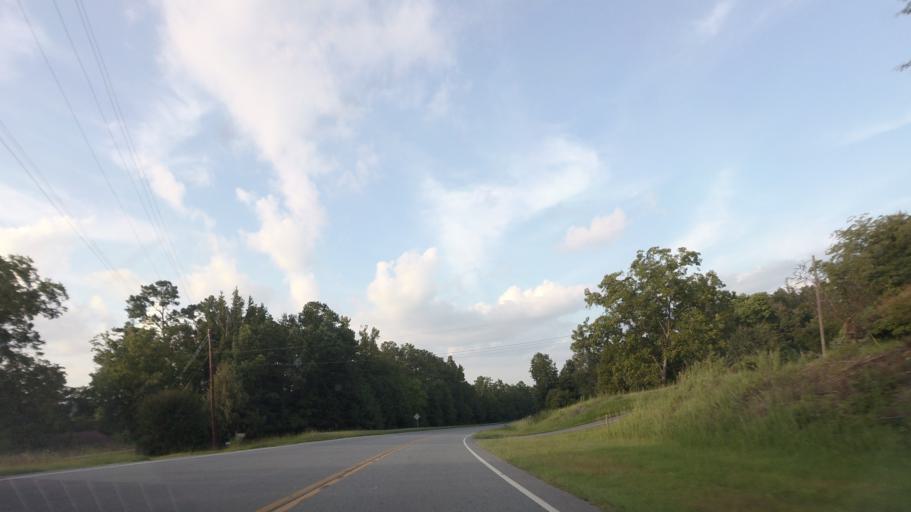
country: US
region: Georgia
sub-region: Wilkinson County
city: Gordon
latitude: 32.8638
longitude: -83.3468
